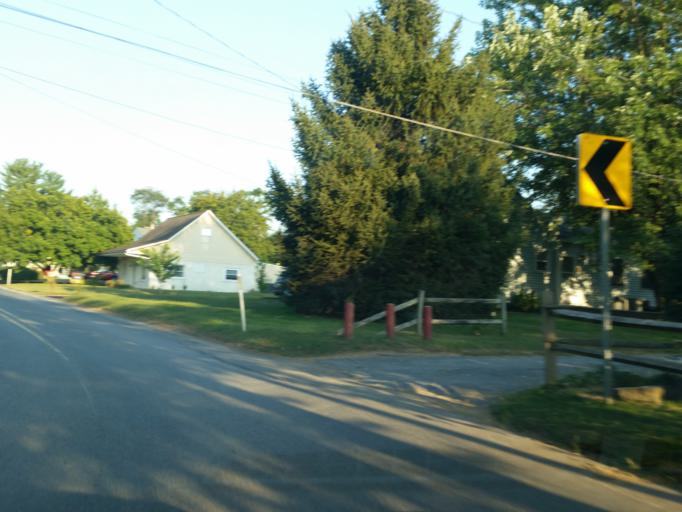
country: US
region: Pennsylvania
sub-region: Lebanon County
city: Cleona
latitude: 40.3693
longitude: -76.4816
